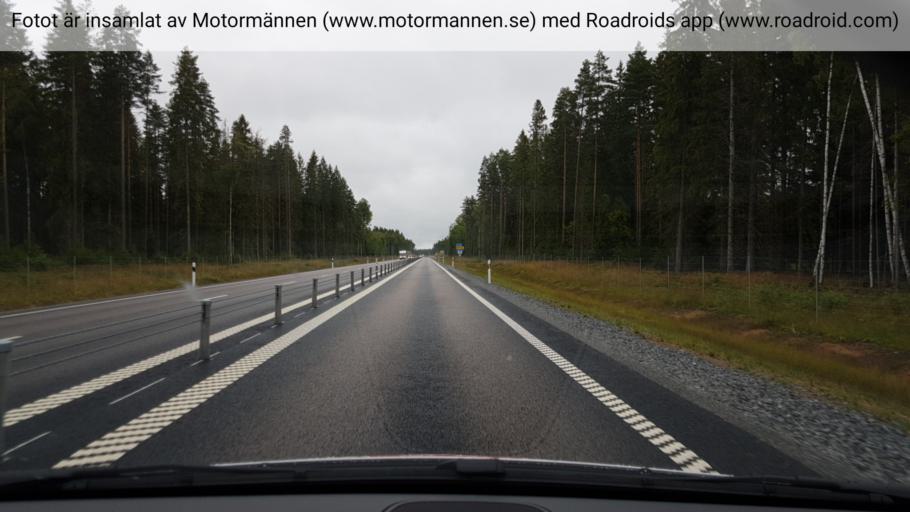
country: SE
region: Uppsala
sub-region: Heby Kommun
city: Tarnsjo
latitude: 60.0582
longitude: 16.8959
